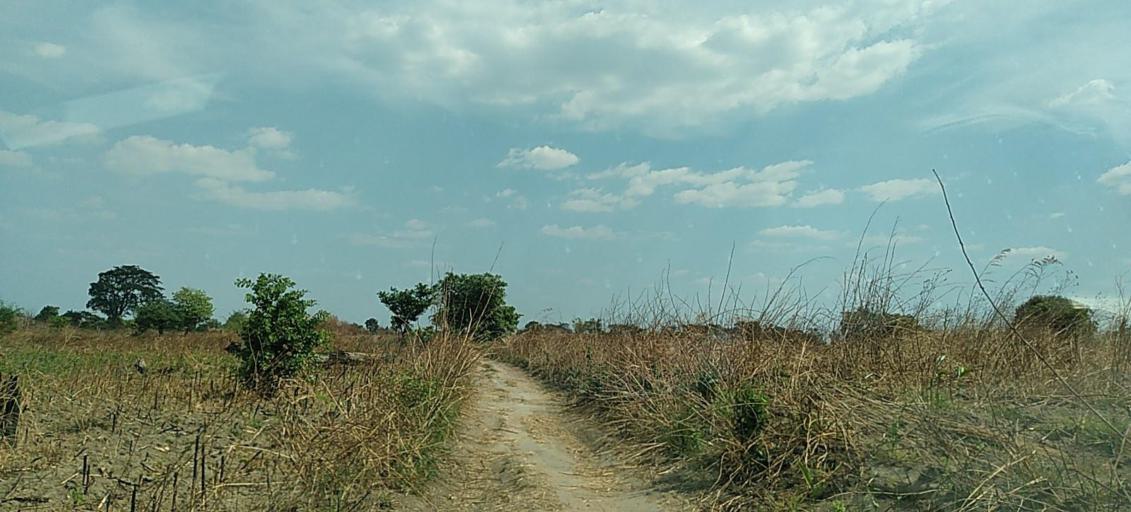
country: ZM
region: Copperbelt
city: Chililabombwe
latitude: -12.3489
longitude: 27.7934
